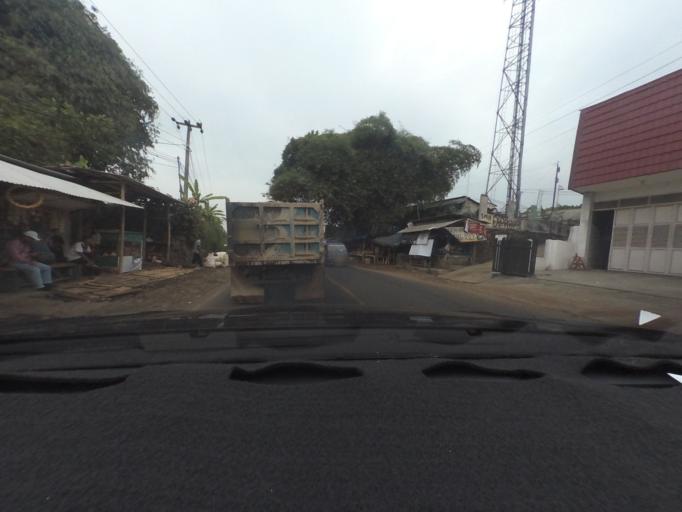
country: ID
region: West Java
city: Cicurug
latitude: -6.8139
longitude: 106.7686
